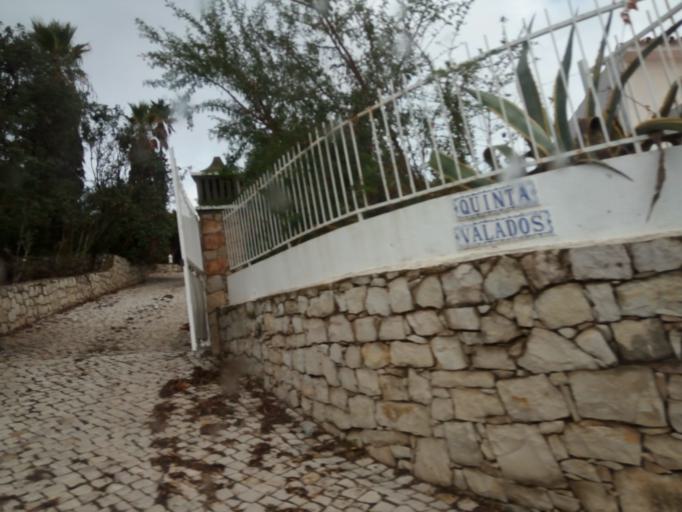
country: PT
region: Faro
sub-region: Faro
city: Santa Barbara de Nexe
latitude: 37.1050
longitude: -7.9995
